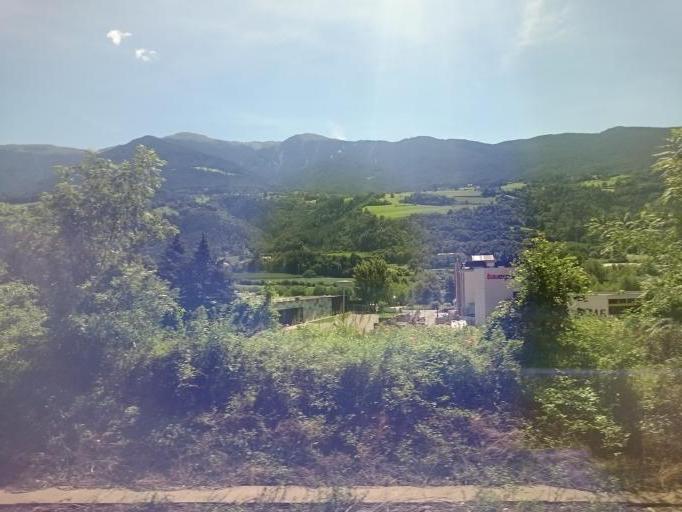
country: IT
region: Trentino-Alto Adige
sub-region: Bolzano
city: Bressanone
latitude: 46.7028
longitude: 11.6480
